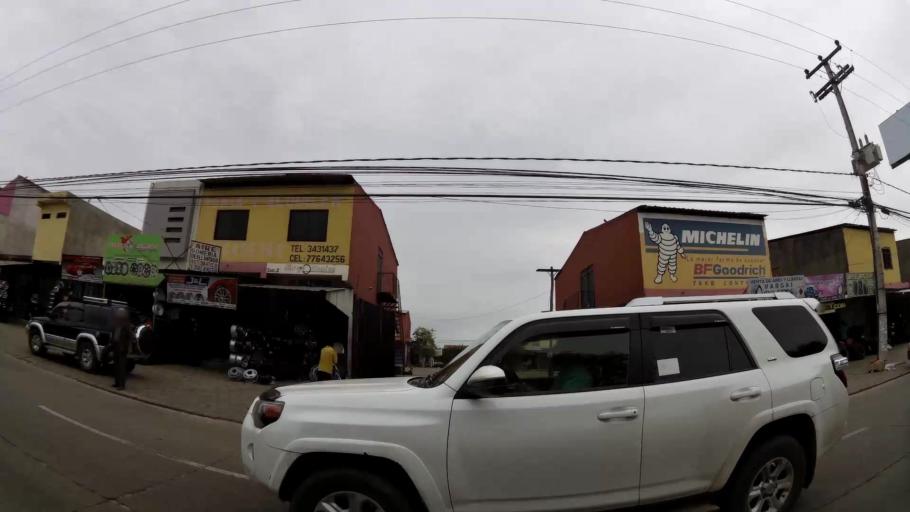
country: BO
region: Santa Cruz
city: Santa Cruz de la Sierra
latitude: -17.8079
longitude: -63.2116
